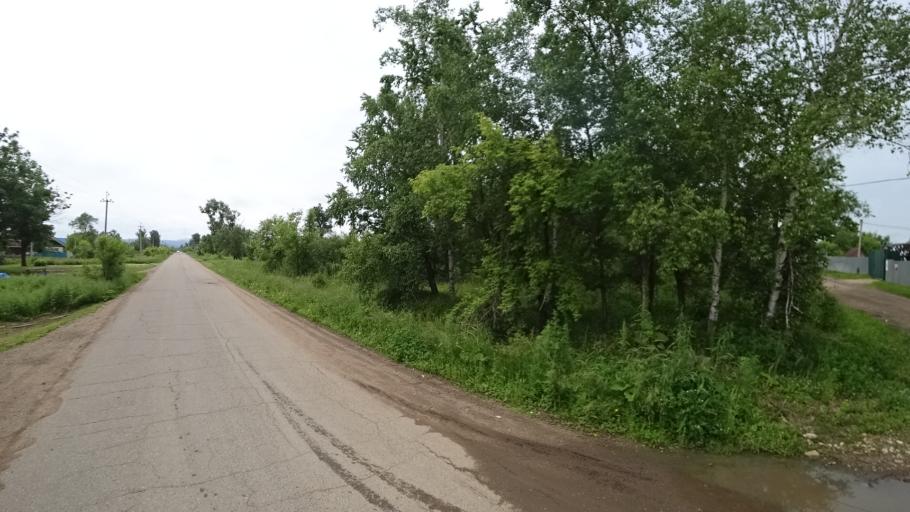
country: RU
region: Primorskiy
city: Novosysoyevka
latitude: 44.2431
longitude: 133.3675
